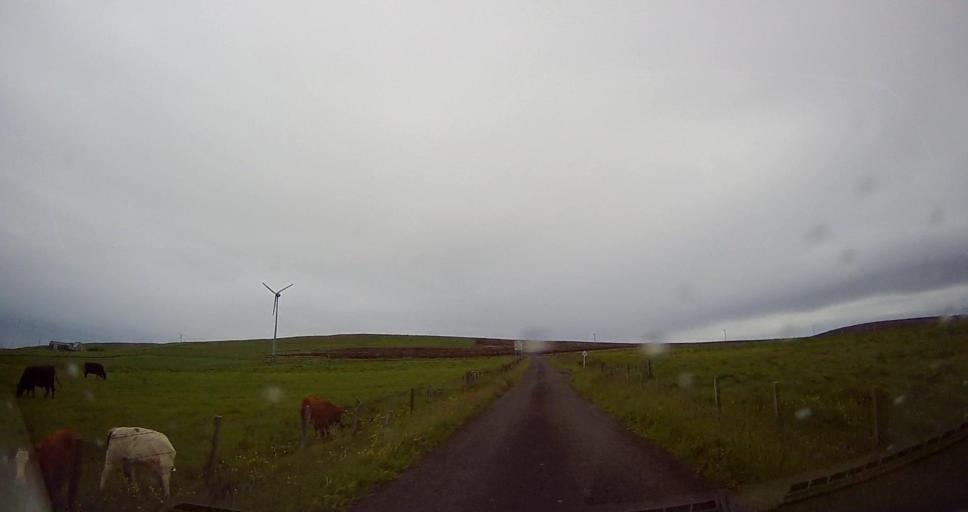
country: GB
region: Scotland
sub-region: Orkney Islands
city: Stromness
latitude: 59.0908
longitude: -3.1829
